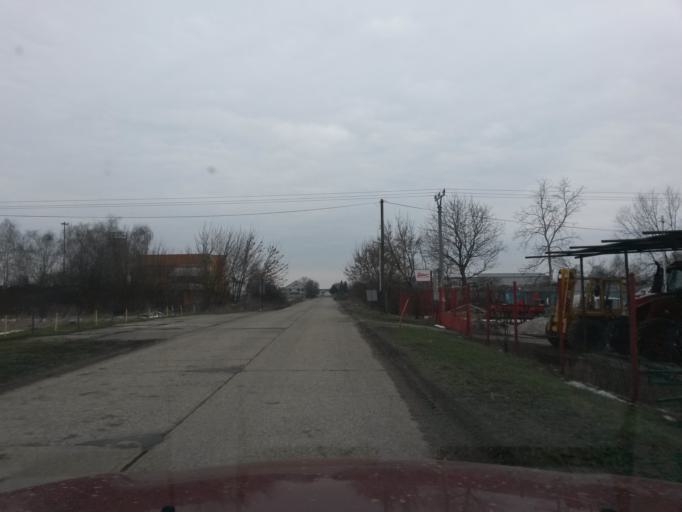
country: SK
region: Kosicky
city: Michalovce
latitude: 48.7511
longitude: 21.8865
